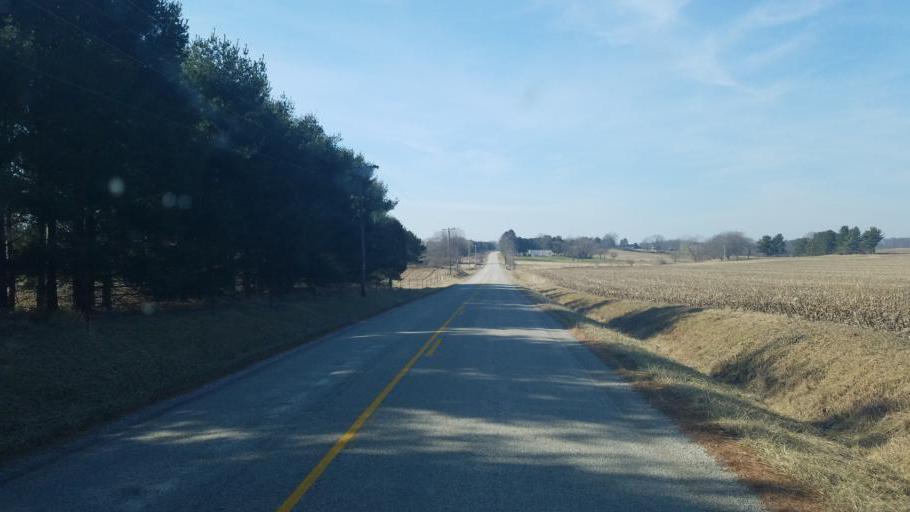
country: US
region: Ohio
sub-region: Ashland County
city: Ashland
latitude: 40.8058
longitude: -82.2501
